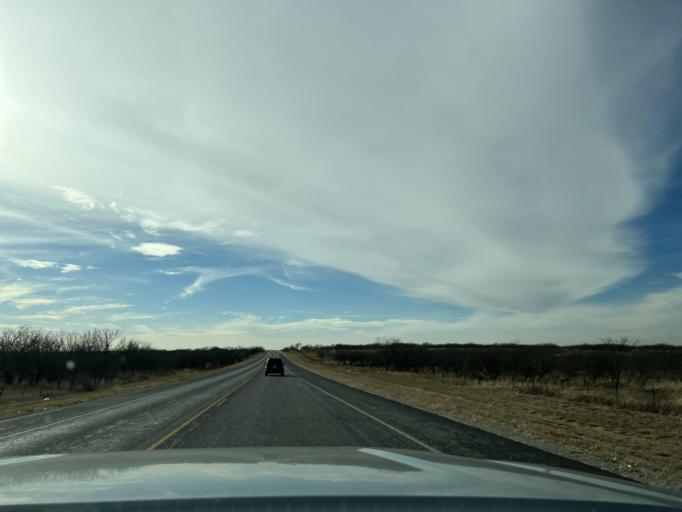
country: US
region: Texas
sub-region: Fisher County
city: Roby
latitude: 32.7552
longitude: -100.3323
